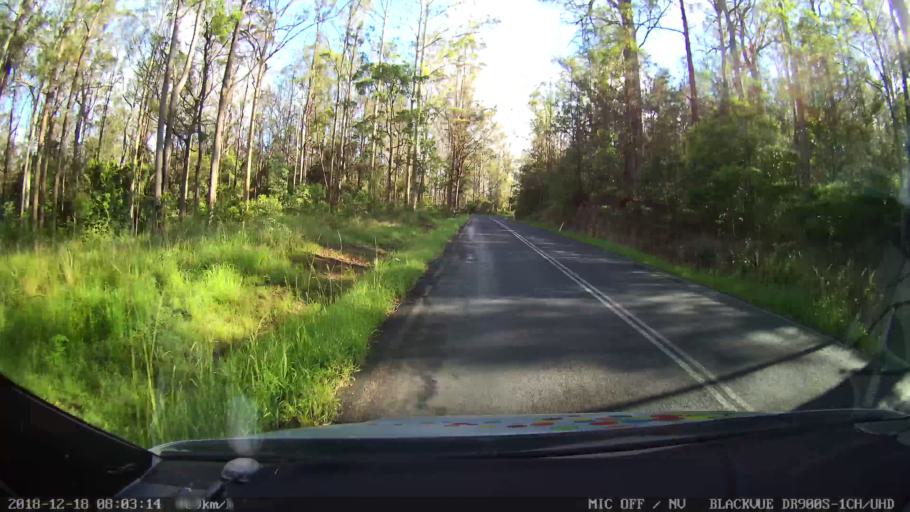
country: AU
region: New South Wales
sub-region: Kyogle
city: Kyogle
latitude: -28.3869
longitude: 152.6391
